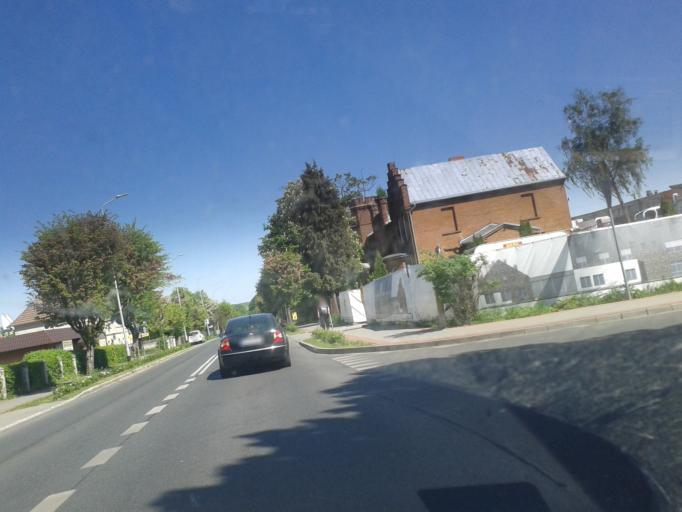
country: PL
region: West Pomeranian Voivodeship
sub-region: Powiat swidwinski
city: Polczyn-Zdroj
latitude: 53.7642
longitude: 16.1011
